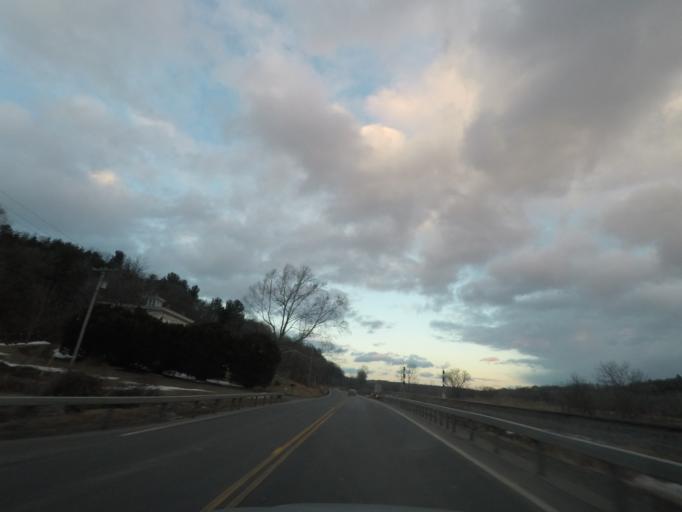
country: US
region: New York
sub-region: Montgomery County
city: Fonda
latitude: 42.9426
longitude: -74.4079
